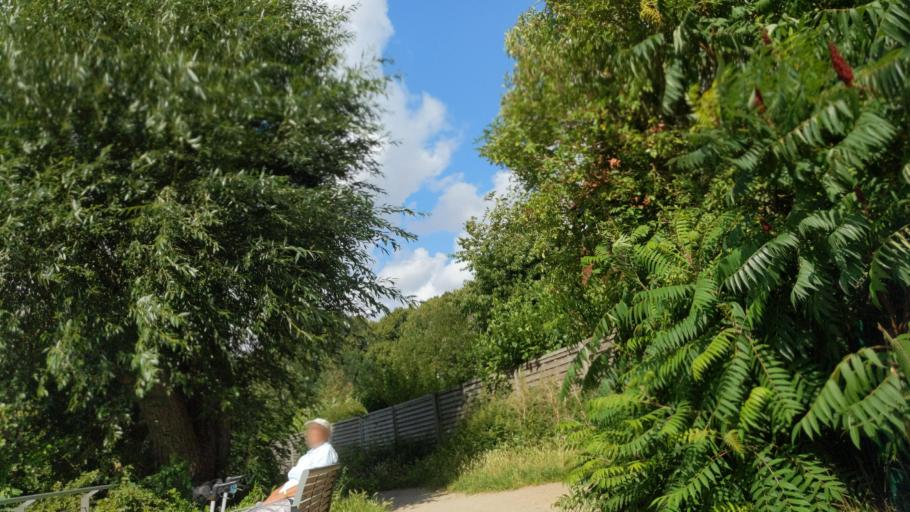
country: DE
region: Schleswig-Holstein
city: Reinfeld
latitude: 53.8337
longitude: 10.4860
